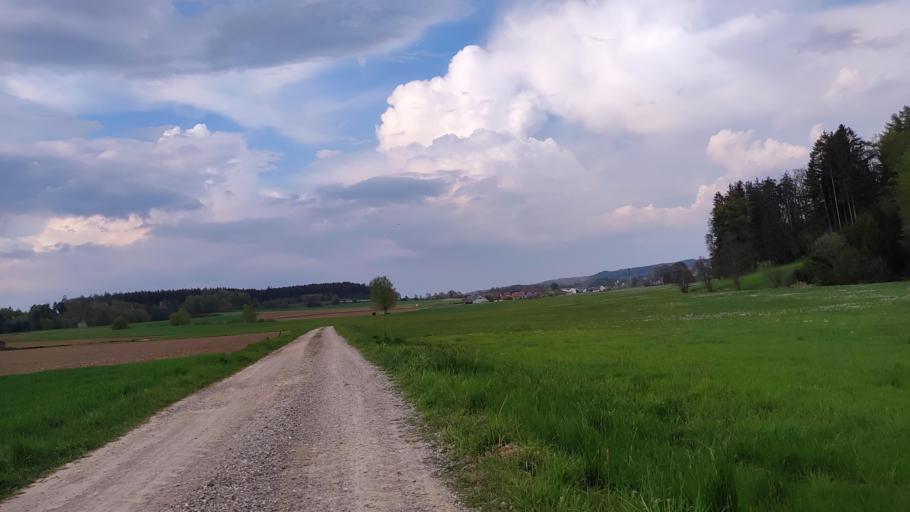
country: DE
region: Bavaria
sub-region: Swabia
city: Zusmarshausen
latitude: 48.3969
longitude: 10.5652
